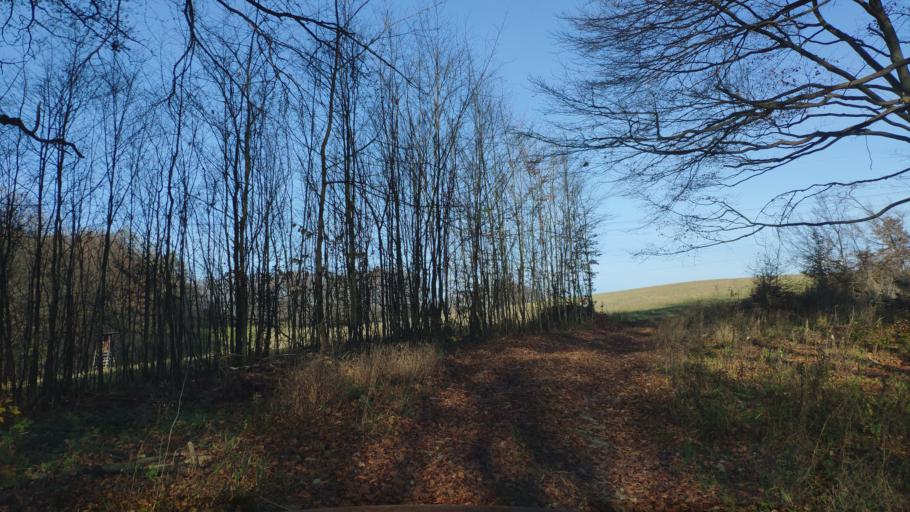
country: SK
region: Presovsky
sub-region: Okres Presov
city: Presov
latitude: 48.8968
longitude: 21.2104
